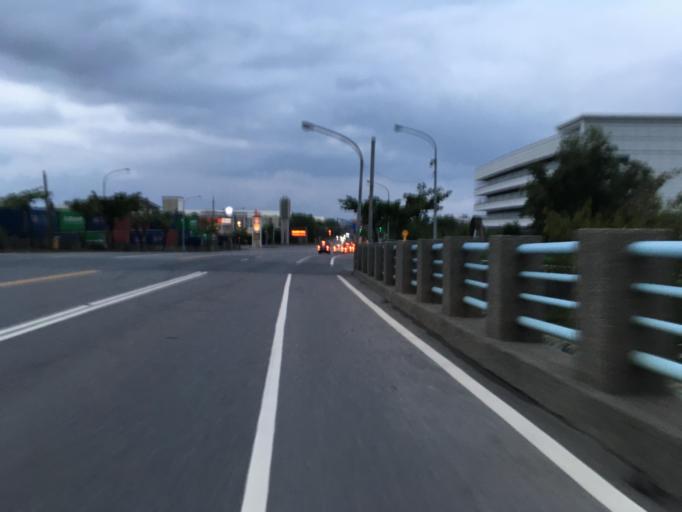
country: TW
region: Taiwan
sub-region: Yilan
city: Yilan
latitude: 24.6323
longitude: 121.8318
